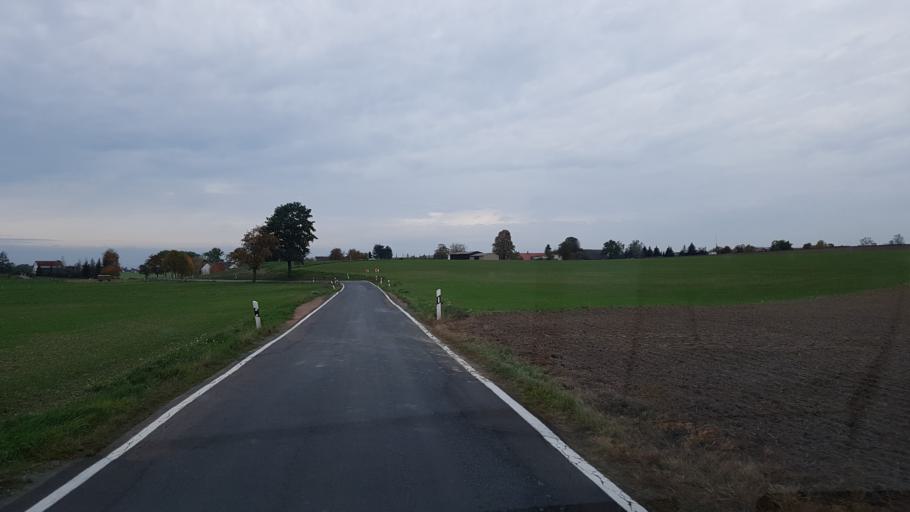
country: DE
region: Saxony
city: Dahlen
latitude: 51.3793
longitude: 12.9535
